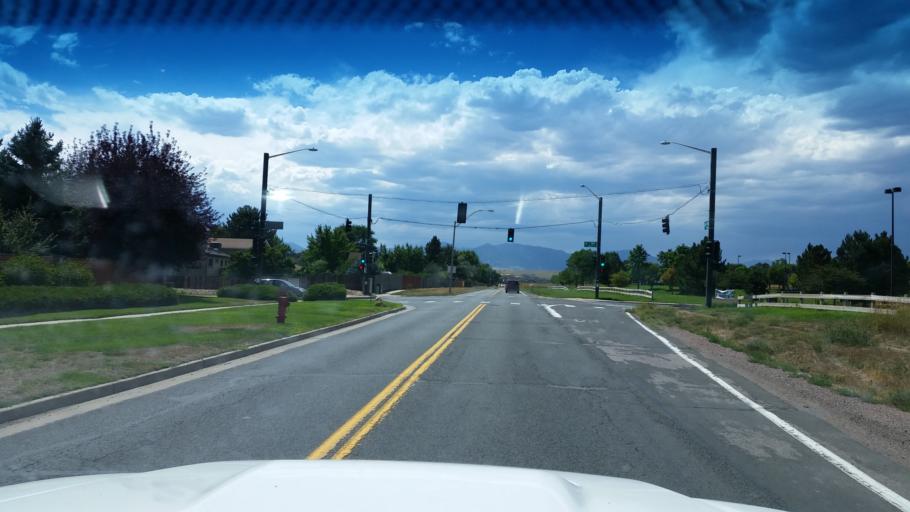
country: US
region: Colorado
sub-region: Broomfield County
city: Broomfield
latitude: 39.8928
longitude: -105.1161
